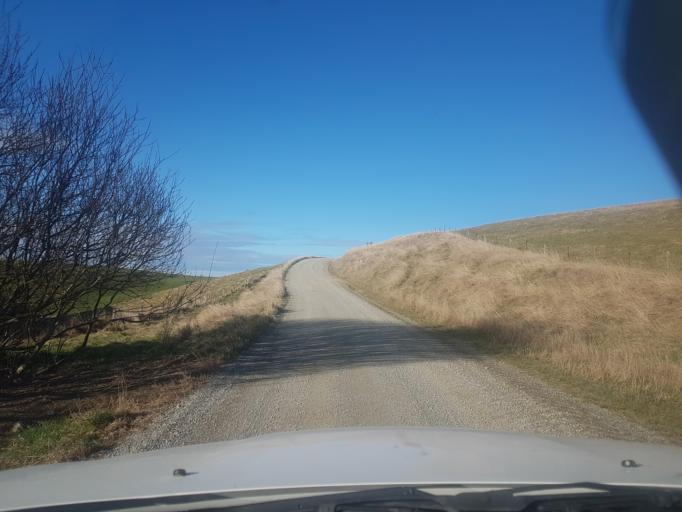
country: NZ
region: Canterbury
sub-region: Timaru District
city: Pleasant Point
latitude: -44.1664
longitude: 170.8992
